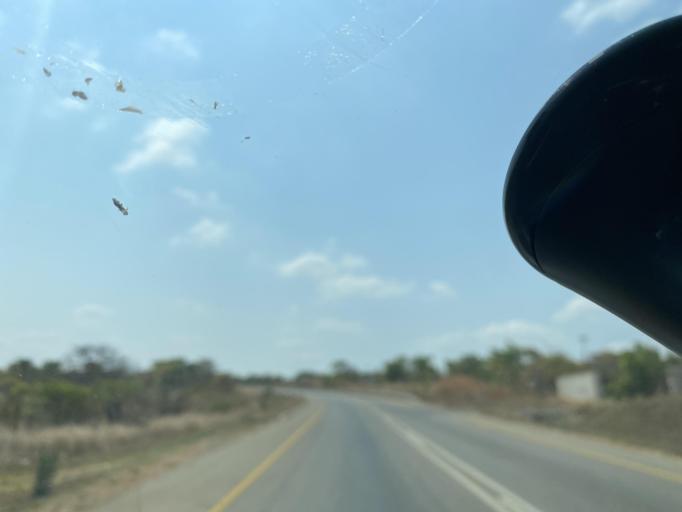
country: ZM
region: Lusaka
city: Chongwe
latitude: -15.5327
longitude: 28.6387
